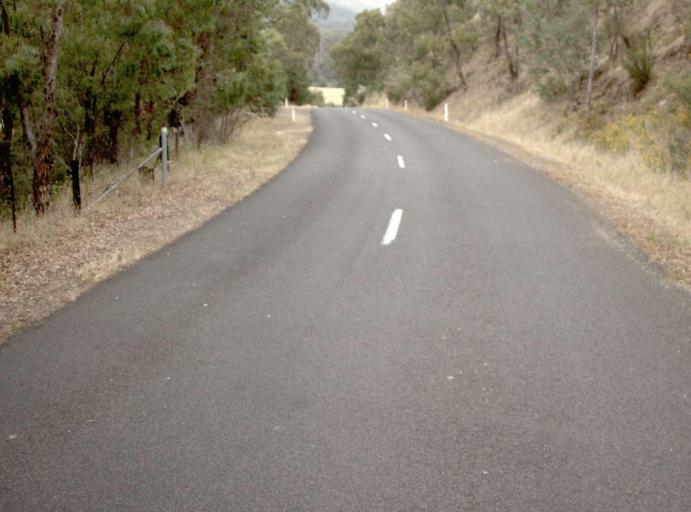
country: AU
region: Victoria
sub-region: Wellington
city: Heyfield
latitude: -37.6934
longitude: 146.6500
